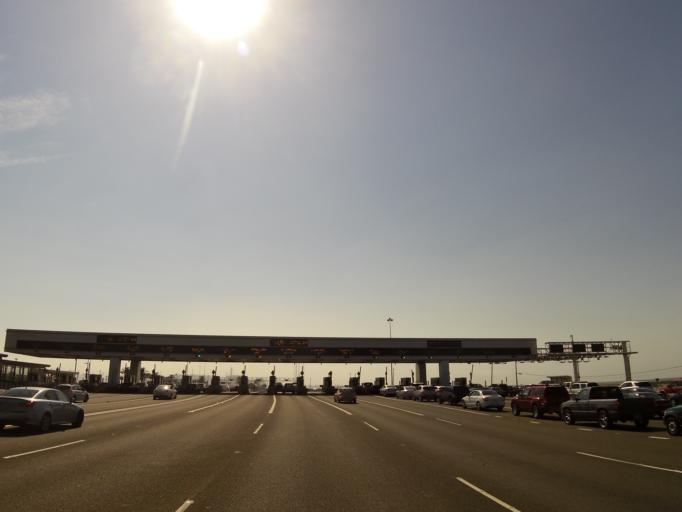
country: US
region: California
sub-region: Alameda County
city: Emeryville
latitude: 37.8252
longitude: -122.3128
